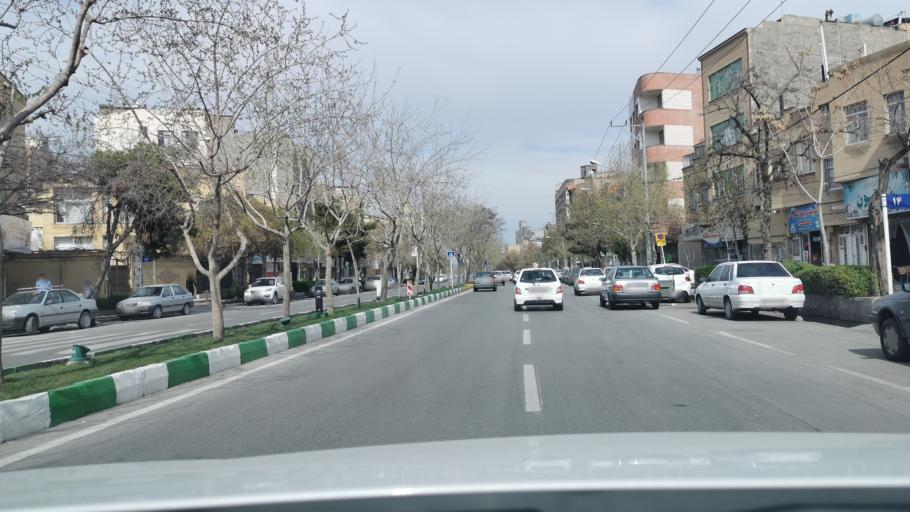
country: IR
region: Razavi Khorasan
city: Mashhad
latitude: 36.3182
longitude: 59.6006
